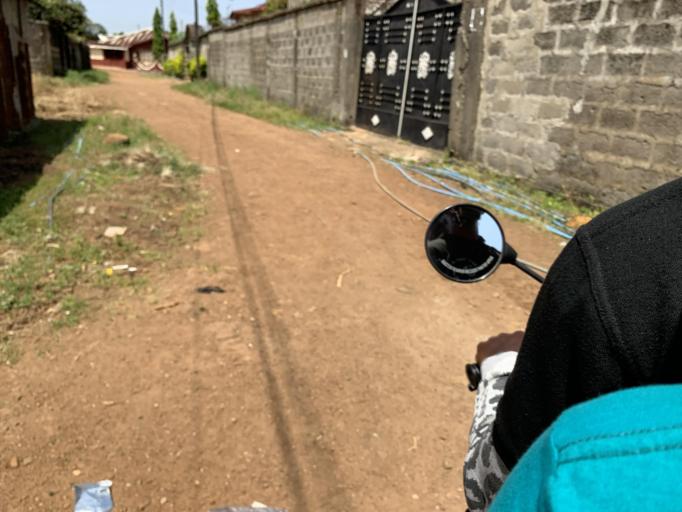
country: SL
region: Western Area
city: Hastings
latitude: 8.3768
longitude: -13.1312
